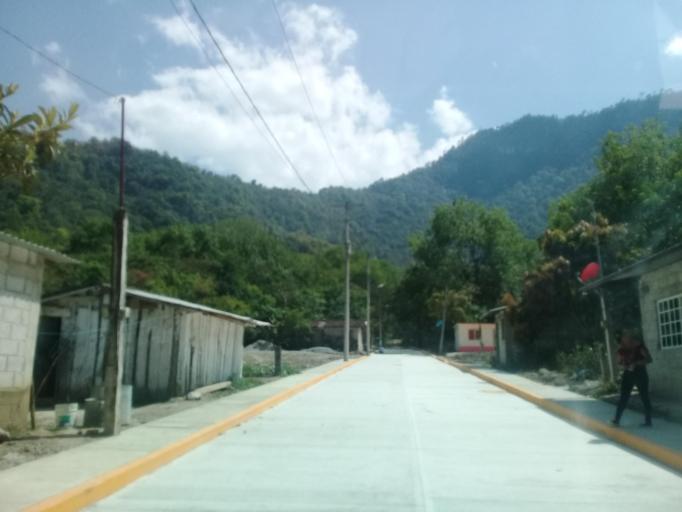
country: MX
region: Veracruz
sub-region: Tlilapan
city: Tonalixco
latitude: 18.8038
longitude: -97.0692
